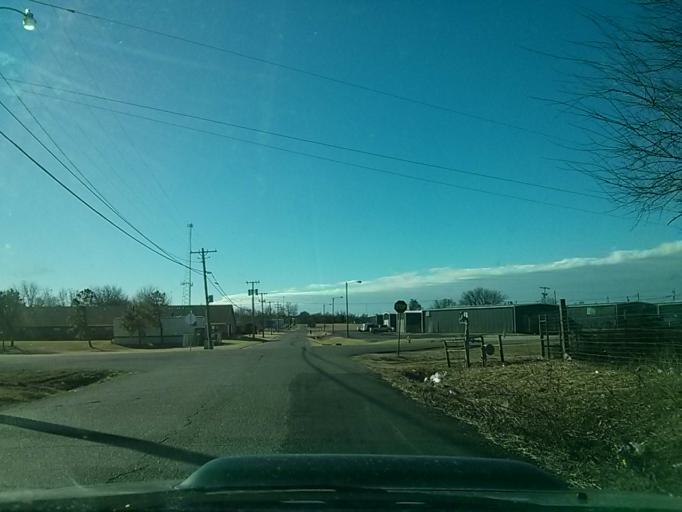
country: US
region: Oklahoma
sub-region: Tulsa County
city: Turley
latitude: 36.2084
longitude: -95.9515
